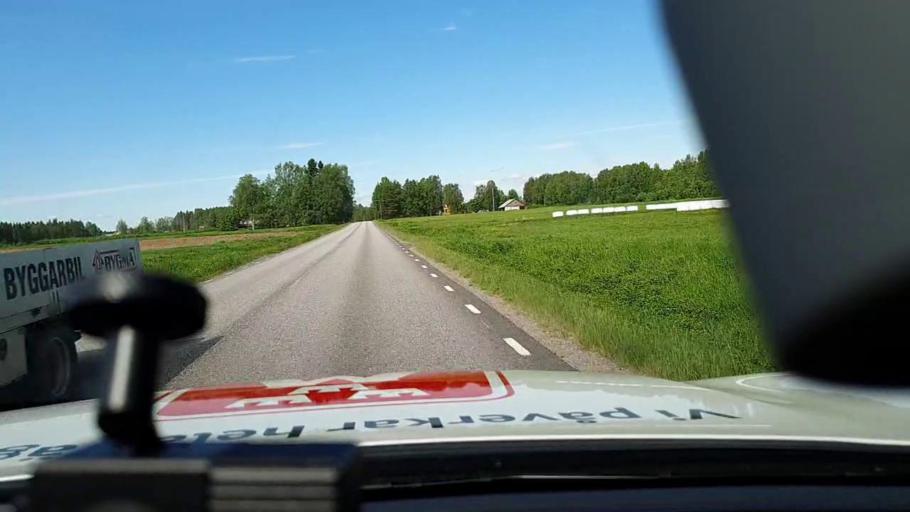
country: SE
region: Norrbotten
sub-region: Lulea Kommun
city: Sodra Sunderbyn
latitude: 65.6535
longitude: 21.8584
